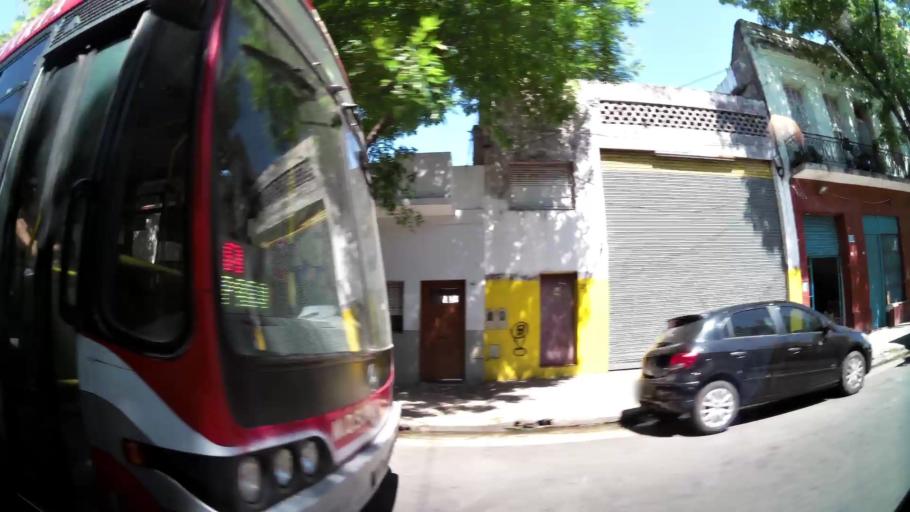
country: AR
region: Buenos Aires F.D.
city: Buenos Aires
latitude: -34.6377
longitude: -58.4190
